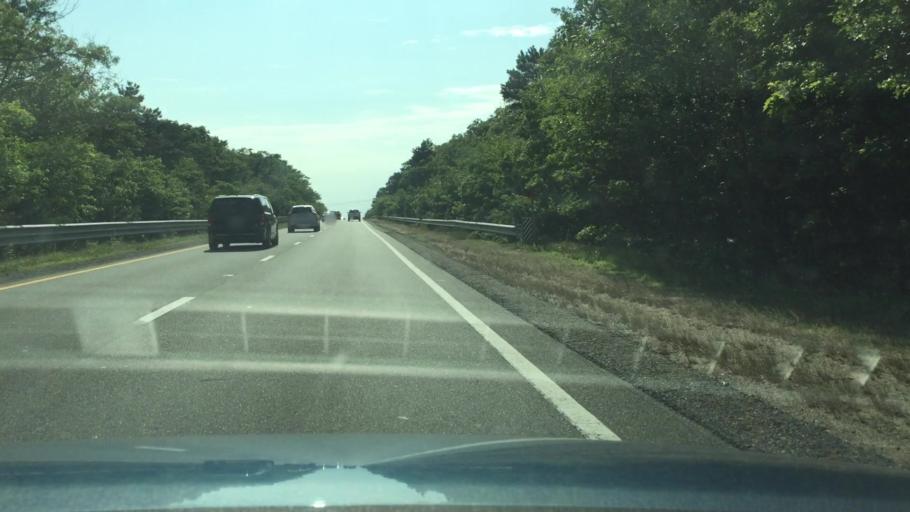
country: US
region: Massachusetts
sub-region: Barnstable County
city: Barnstable
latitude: 41.6881
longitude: -70.2762
